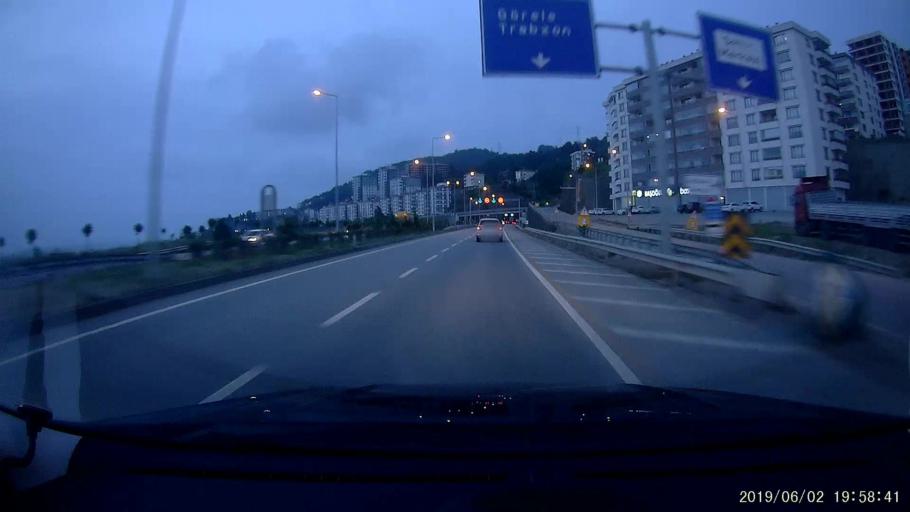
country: TR
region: Giresun
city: Tirebolu
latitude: 40.9995
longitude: 38.8005
